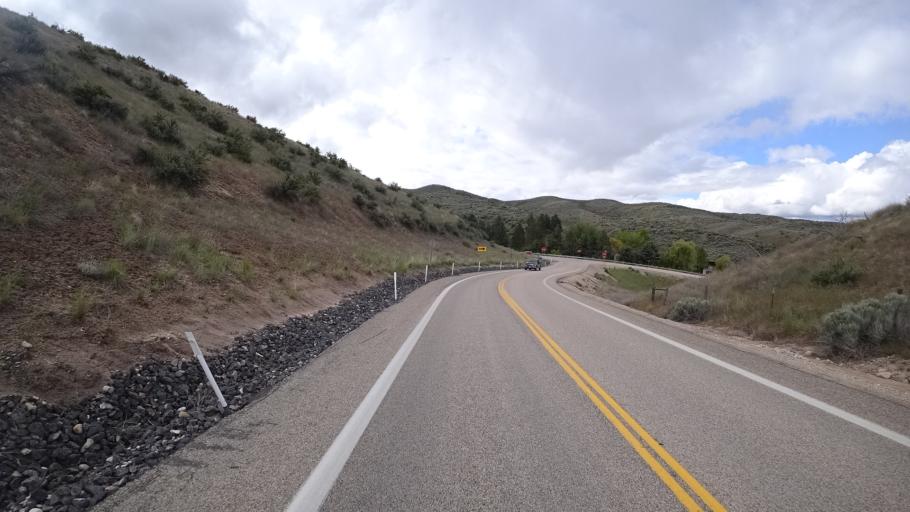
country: US
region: Idaho
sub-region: Ada County
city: Garden City
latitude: 43.6938
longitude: -116.2267
